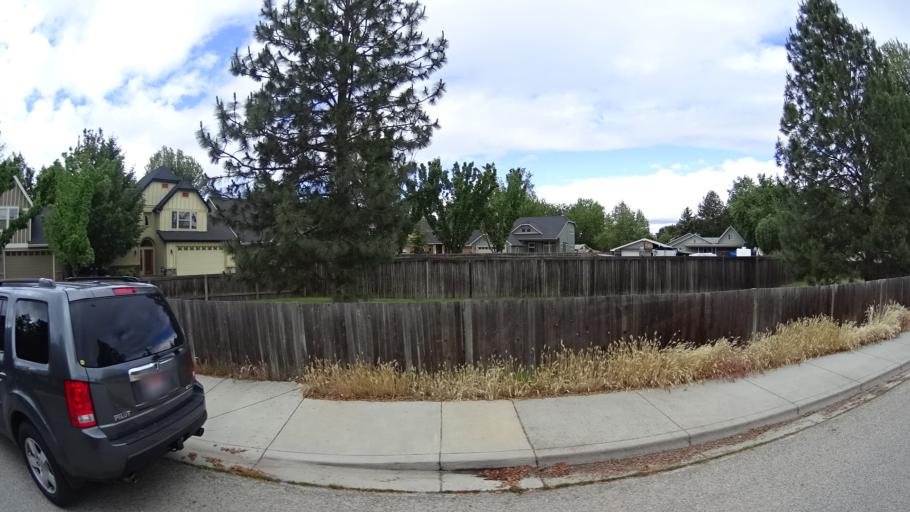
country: US
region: Idaho
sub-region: Ada County
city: Eagle
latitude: 43.6730
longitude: -116.2928
